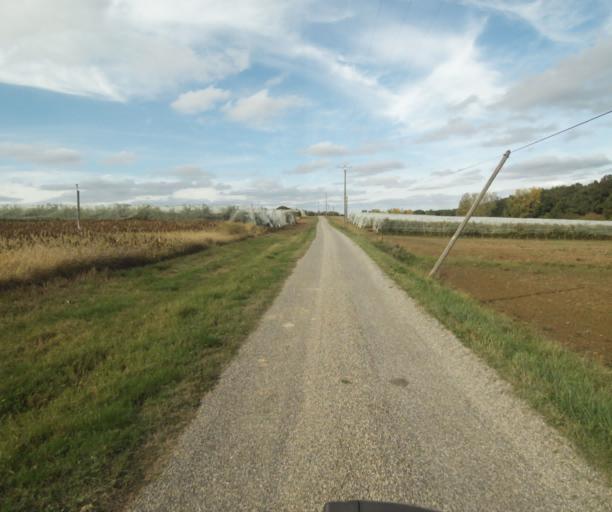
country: FR
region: Midi-Pyrenees
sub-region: Departement du Tarn-et-Garonne
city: Saint-Porquier
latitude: 43.9473
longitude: 1.1335
